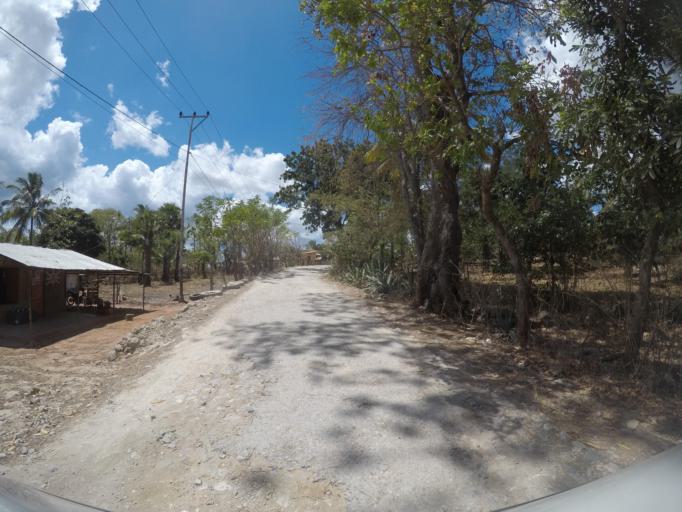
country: TL
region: Baucau
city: Baucau
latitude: -8.4822
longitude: 126.6297
